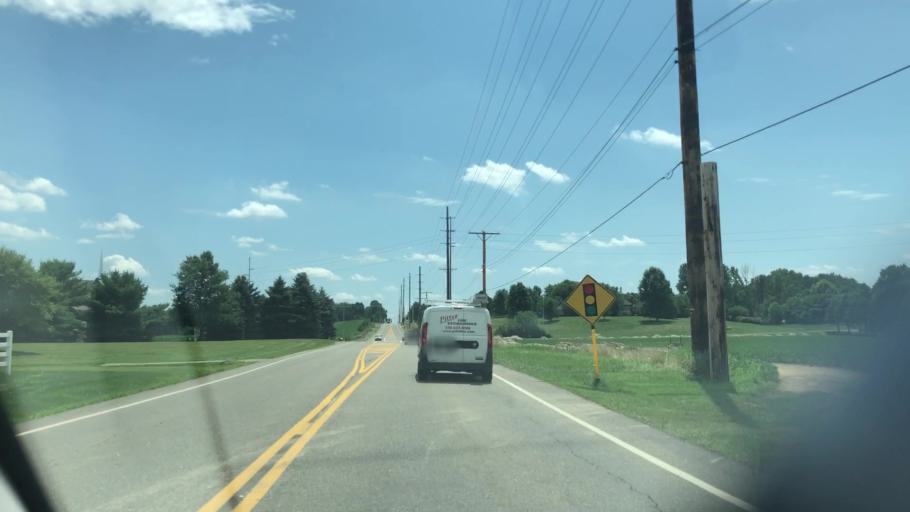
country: US
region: Ohio
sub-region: Summit County
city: Greensburg
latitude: 40.8816
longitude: -81.4993
